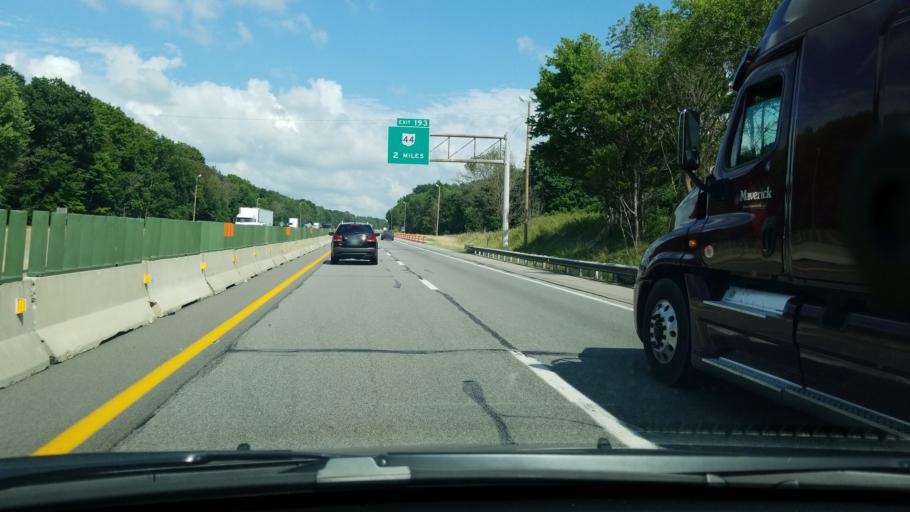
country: US
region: Ohio
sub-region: Portage County
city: Streetsboro
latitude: 41.2479
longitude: -81.2809
